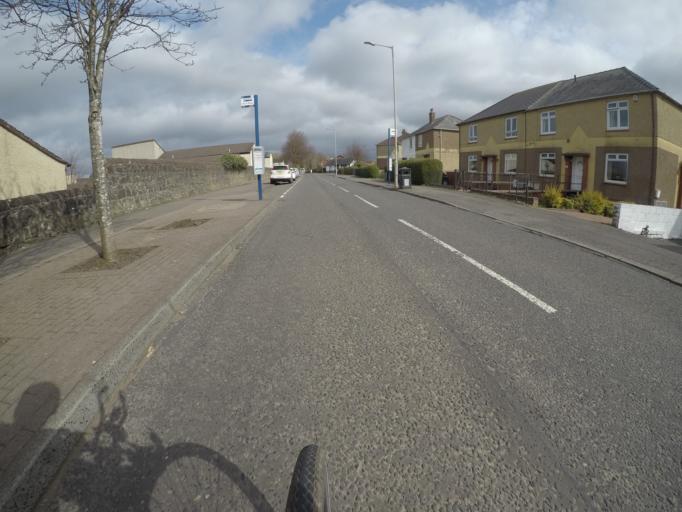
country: GB
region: Scotland
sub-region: North Ayrshire
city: Irvine
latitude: 55.6286
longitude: -4.6382
